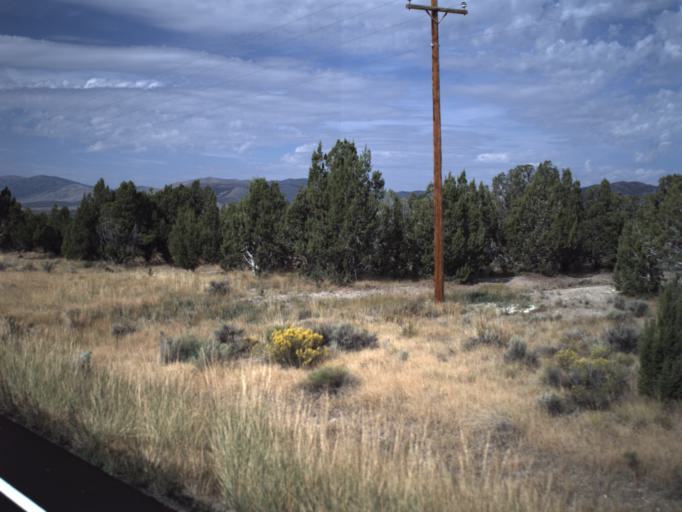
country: US
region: Idaho
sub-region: Cassia County
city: Burley
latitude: 41.8146
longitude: -113.4370
